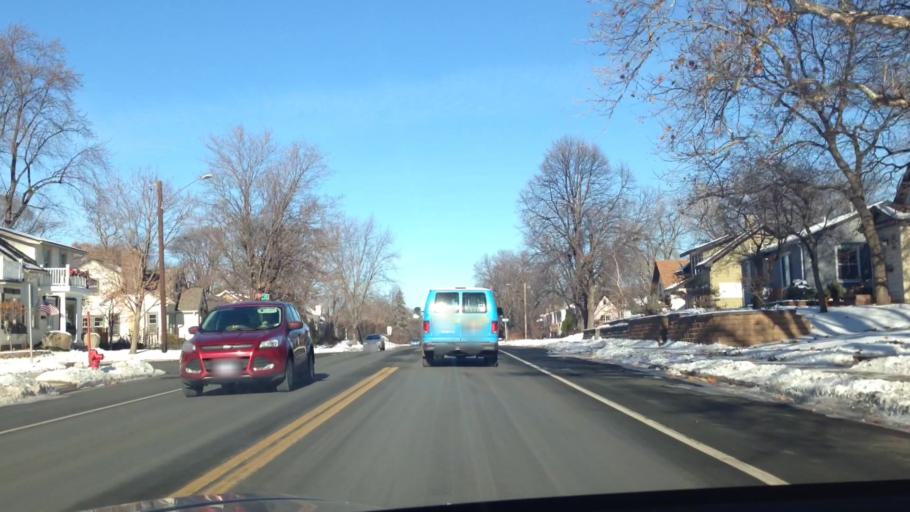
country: US
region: Minnesota
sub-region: Hennepin County
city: Saint Louis Park
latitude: 44.9457
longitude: -93.3604
